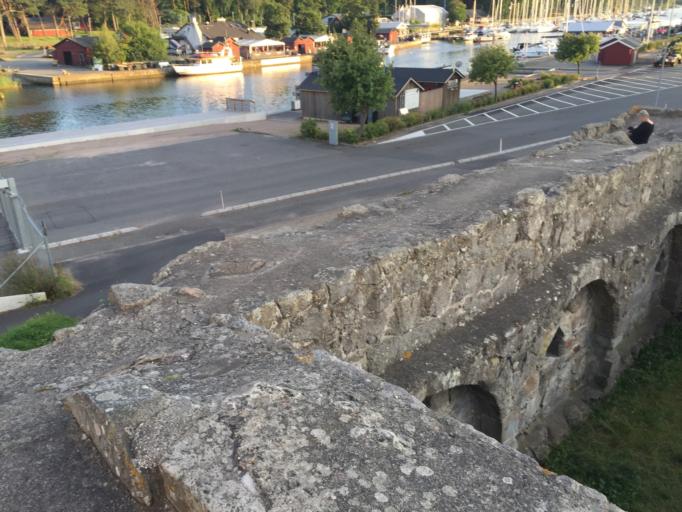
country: SE
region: Skane
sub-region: Kristianstads Kommun
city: Ahus
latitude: 55.9264
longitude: 14.3051
